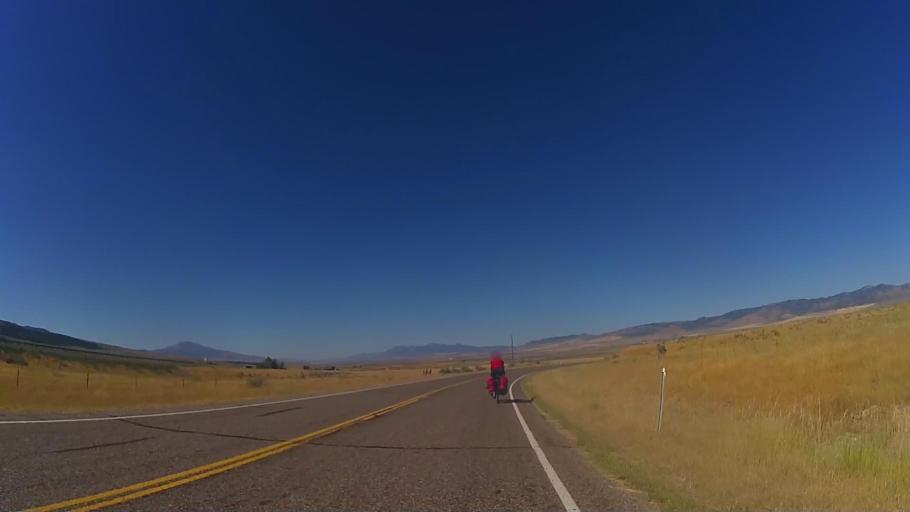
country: US
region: Idaho
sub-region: Oneida County
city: Malad City
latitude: 42.3747
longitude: -112.2085
